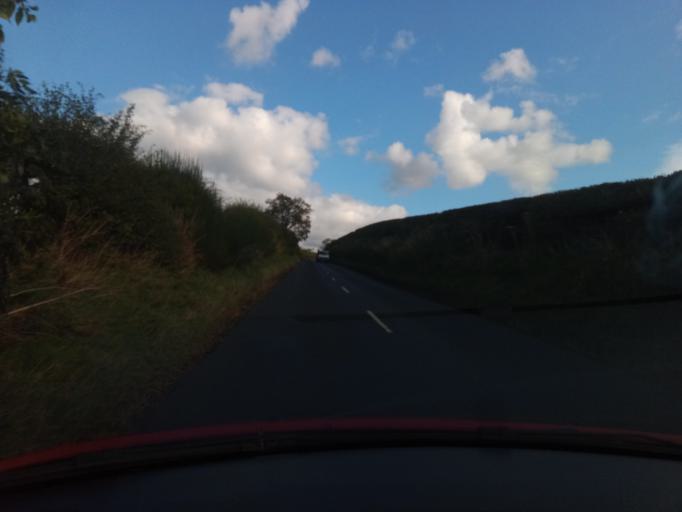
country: GB
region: Scotland
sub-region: The Scottish Borders
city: Kelso
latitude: 55.5712
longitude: -2.3745
